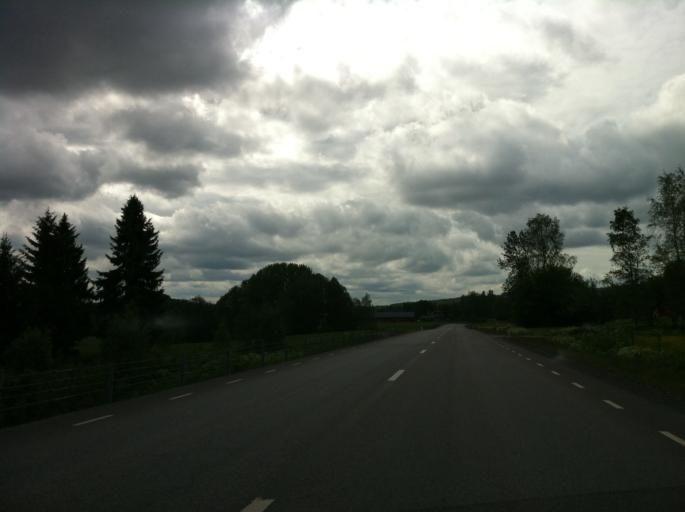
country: SE
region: Vaermland
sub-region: Sunne Kommun
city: Sunne
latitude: 59.7954
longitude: 13.1061
